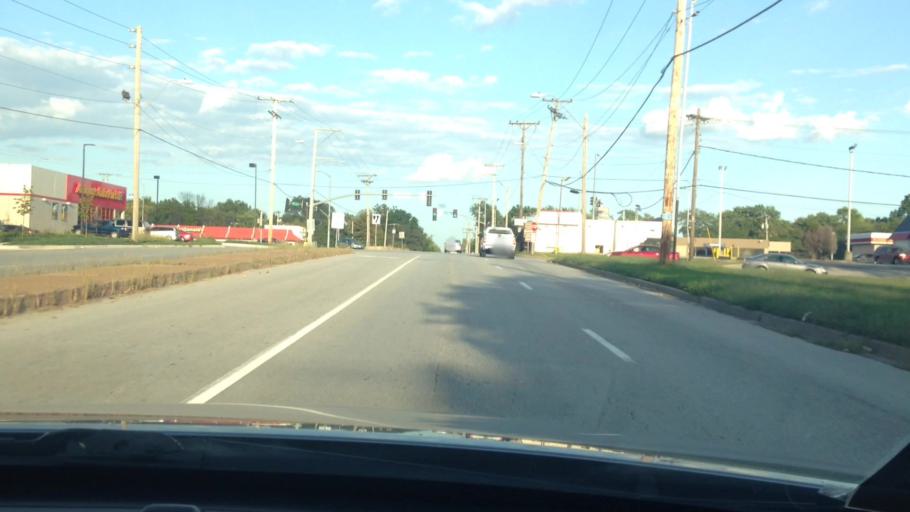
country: US
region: Missouri
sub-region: Jackson County
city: Raytown
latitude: 38.9664
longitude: -94.5011
